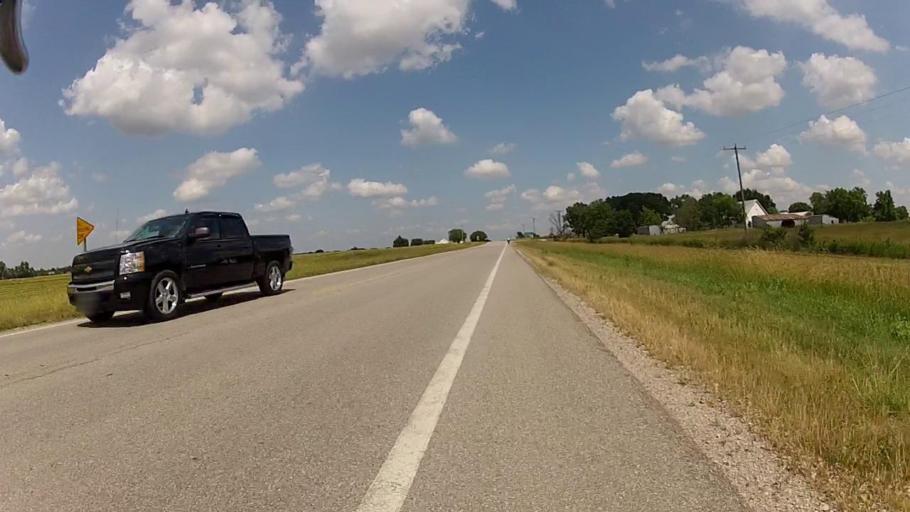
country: US
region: Kansas
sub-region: Labette County
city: Oswego
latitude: 37.1936
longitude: -95.1789
